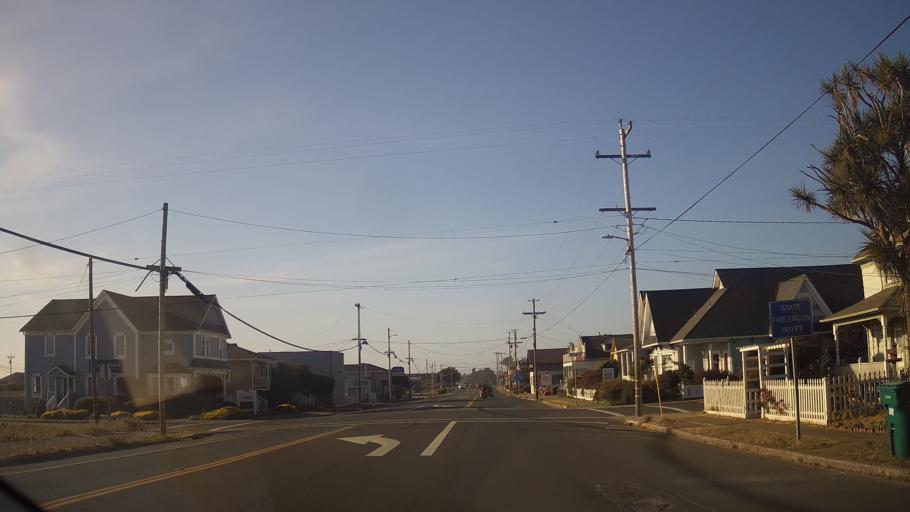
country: US
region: California
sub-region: Mendocino County
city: Fort Bragg
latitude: 39.4489
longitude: -123.8059
